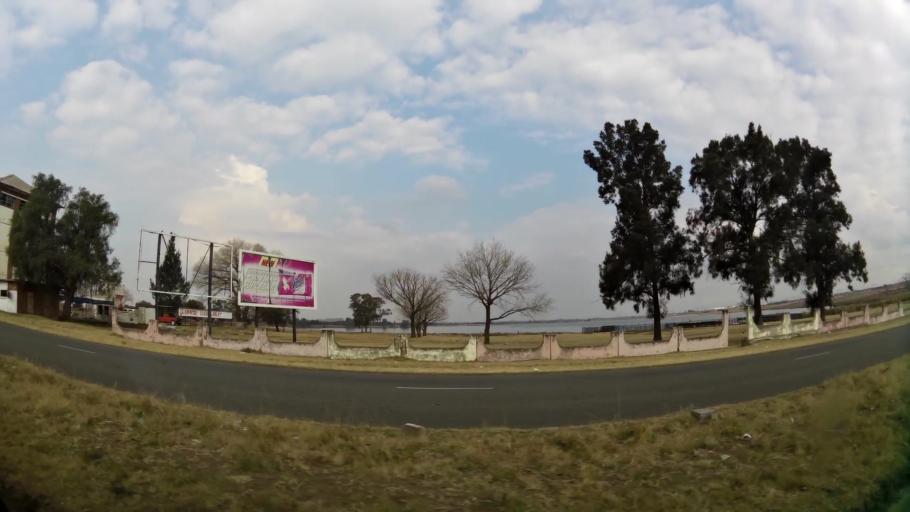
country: ZA
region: Gauteng
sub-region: Sedibeng District Municipality
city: Vereeniging
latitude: -26.6774
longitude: 27.8903
